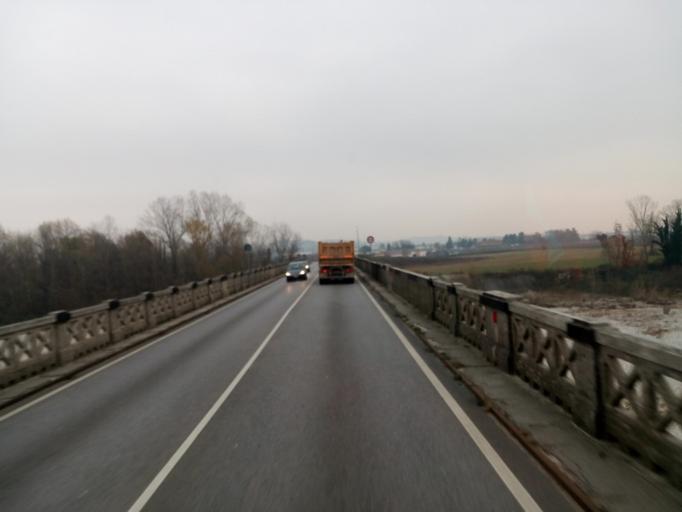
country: IT
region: Friuli Venezia Giulia
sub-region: Provincia di Udine
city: Pradamano
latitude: 46.0166
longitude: 13.3114
